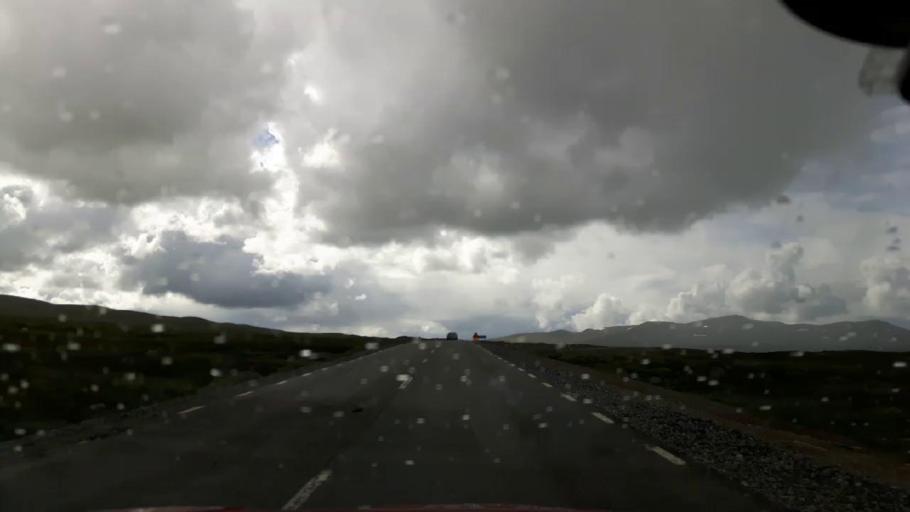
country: NO
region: Nordland
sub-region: Hattfjelldal
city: Hattfjelldal
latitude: 65.0989
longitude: 14.4674
